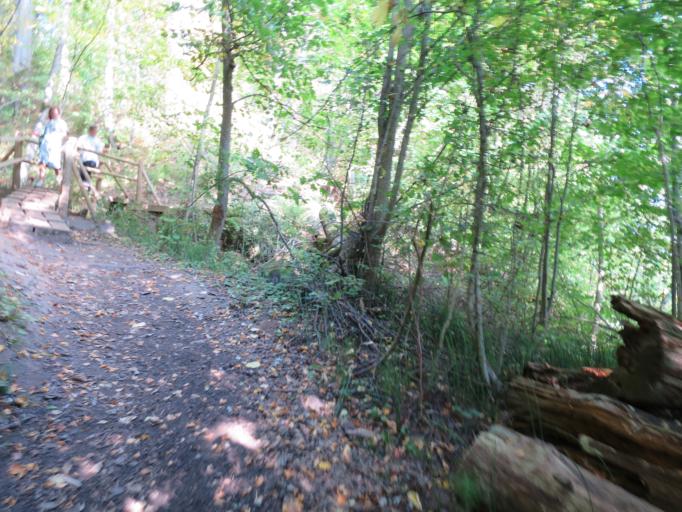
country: LV
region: Sigulda
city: Sigulda
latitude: 57.1501
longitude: 24.8096
